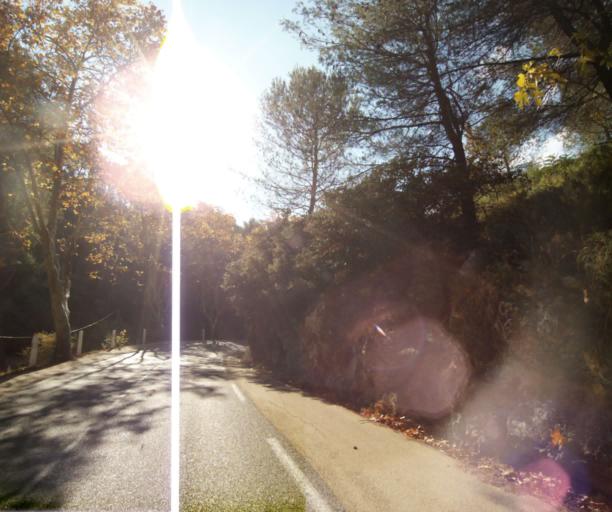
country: FR
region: Provence-Alpes-Cote d'Azur
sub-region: Departement des Bouches-du-Rhone
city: Allauch
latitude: 43.3686
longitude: 5.5026
